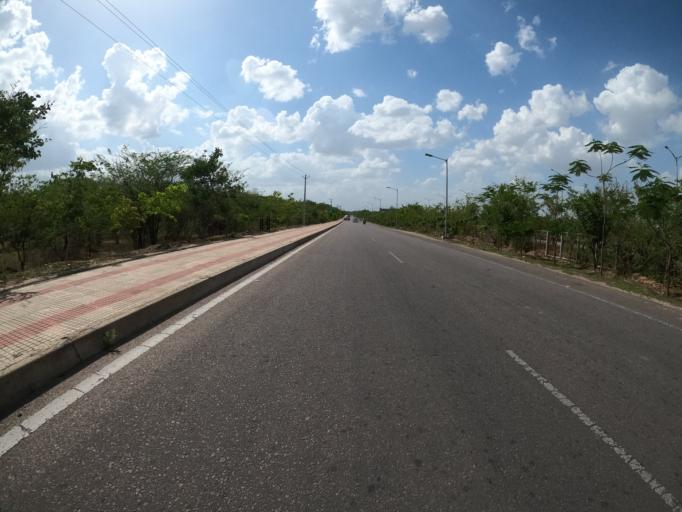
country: IN
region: Telangana
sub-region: Hyderabad
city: Hyderabad
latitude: 17.3662
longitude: 78.3514
